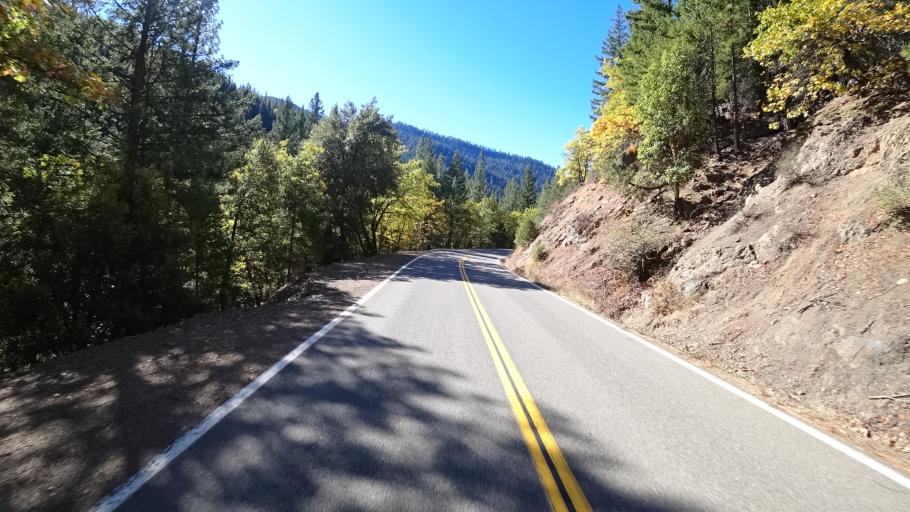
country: US
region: California
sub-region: Trinity County
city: Weaverville
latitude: 41.2188
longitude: -123.0236
